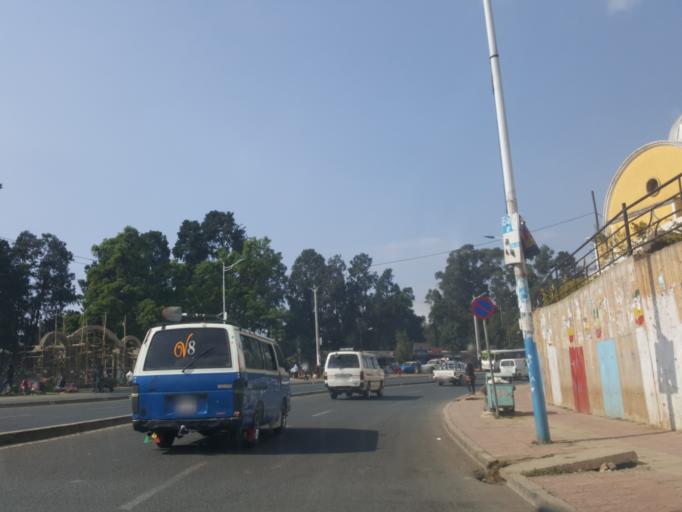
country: ET
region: Adis Abeba
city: Addis Ababa
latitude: 9.0547
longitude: 38.7157
